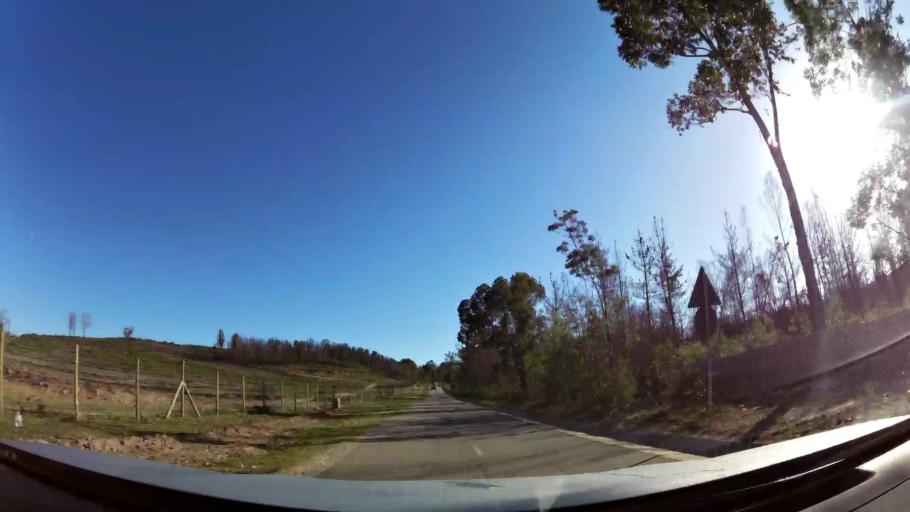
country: ZA
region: Western Cape
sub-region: Eden District Municipality
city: Knysna
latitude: -34.0286
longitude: 23.0098
